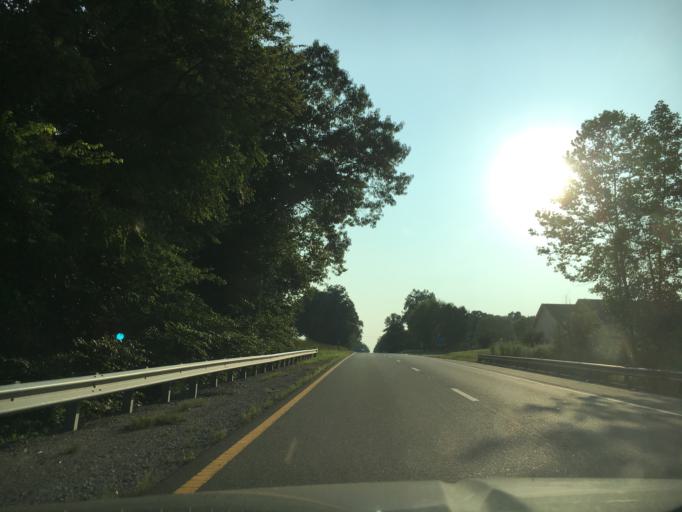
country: US
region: Virginia
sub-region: Prince Edward County
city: Hampden Sydney
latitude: 37.3122
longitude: -78.4947
